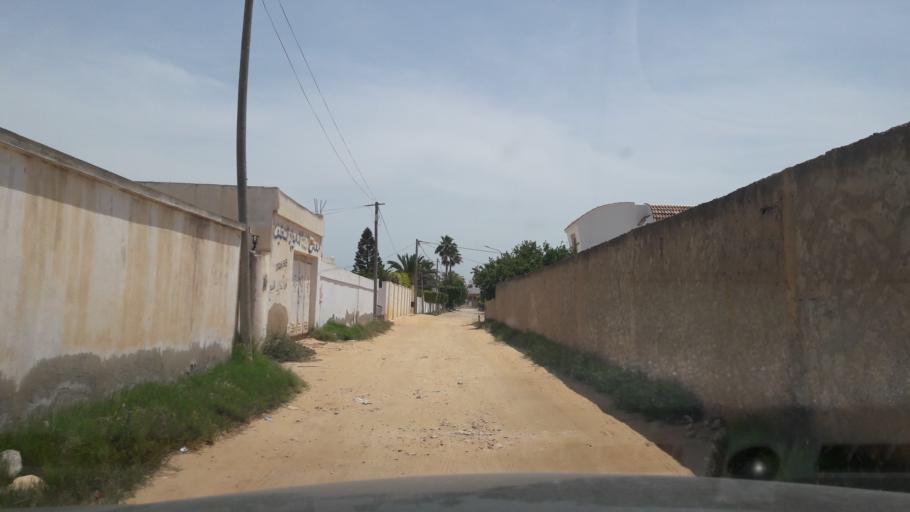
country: TN
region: Safaqis
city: Sfax
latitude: 34.7794
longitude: 10.7562
